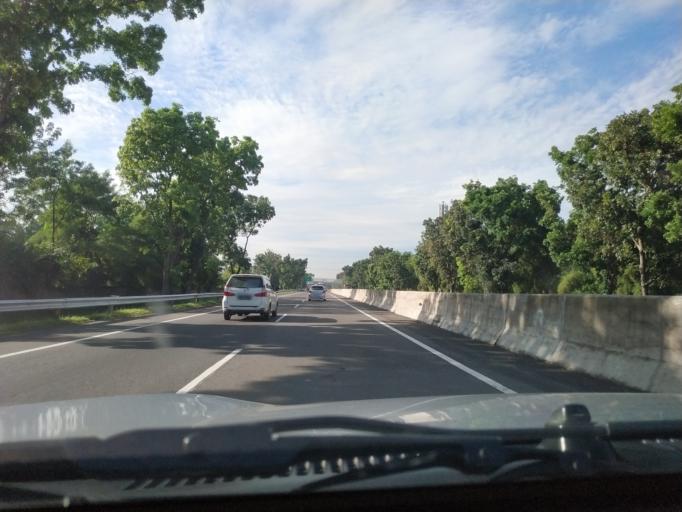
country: ID
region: North Sumatra
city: Deli Tua
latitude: 3.5549
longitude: 98.7253
